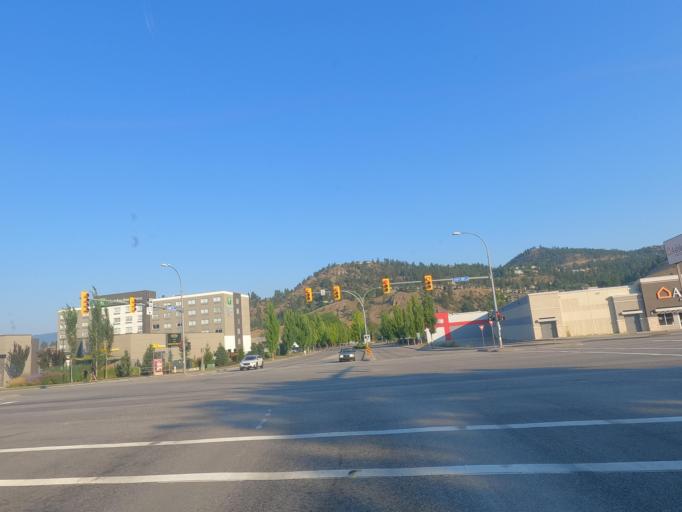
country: CA
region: British Columbia
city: Kelowna
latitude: 49.8894
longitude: -119.4202
